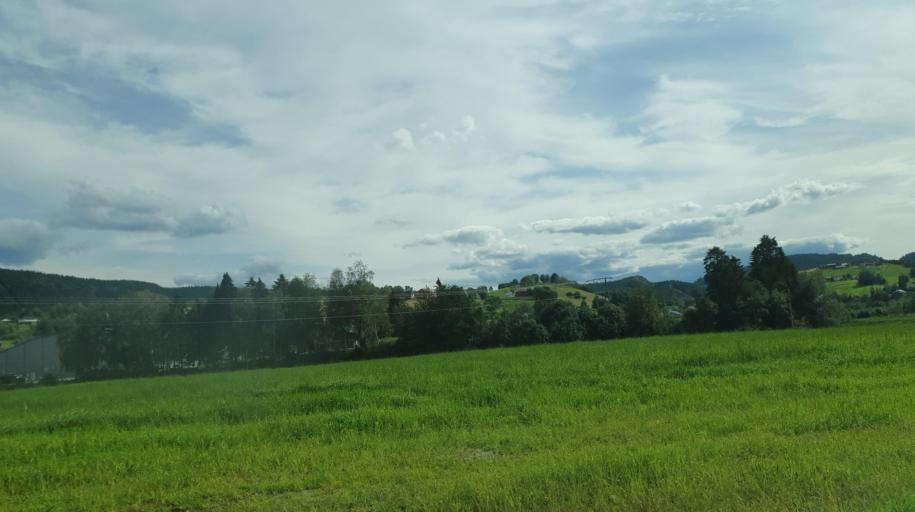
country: NO
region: Sor-Trondelag
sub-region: Selbu
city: Mebonden
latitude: 63.2518
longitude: 11.0896
